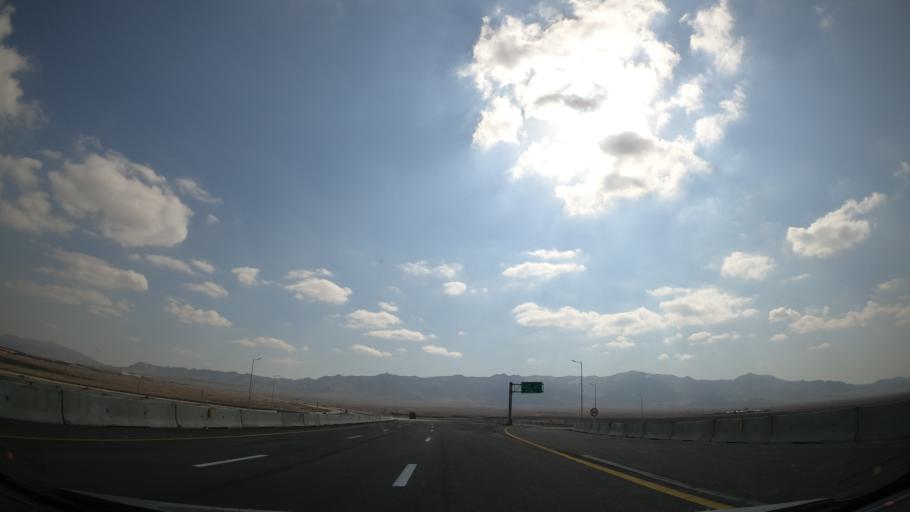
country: IR
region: Alborz
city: Eshtehard
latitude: 35.7314
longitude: 50.5607
